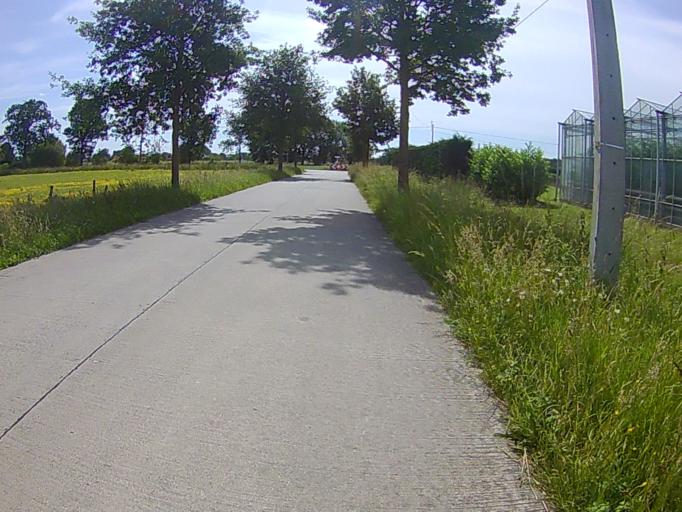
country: BE
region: Flanders
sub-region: Provincie Antwerpen
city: Lier
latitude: 51.0900
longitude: 4.5955
